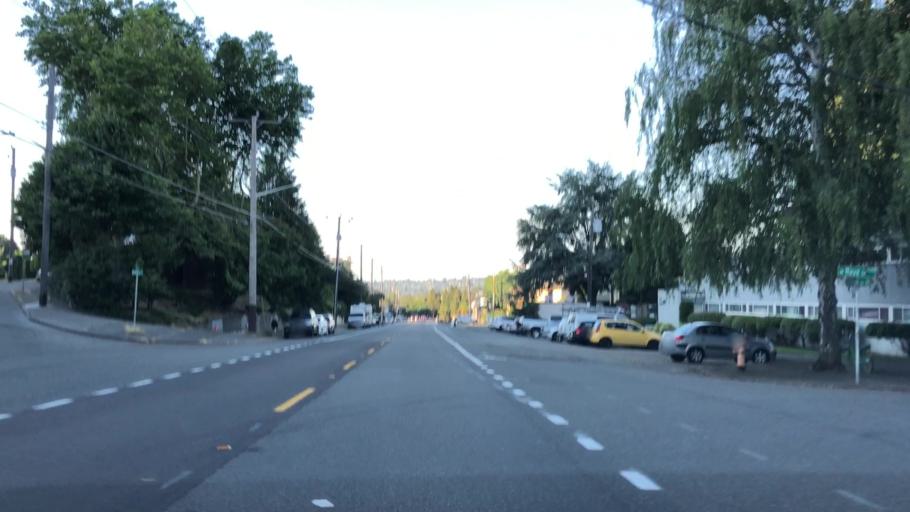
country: US
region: Washington
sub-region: King County
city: Seattle
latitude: 47.6429
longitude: -122.3846
